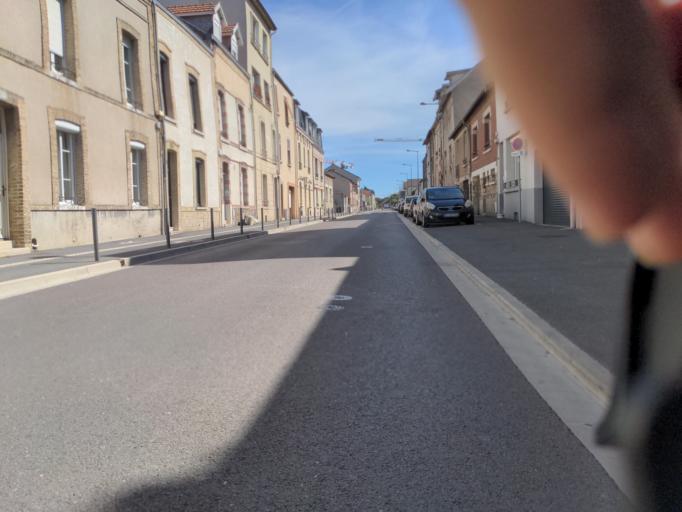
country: FR
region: Champagne-Ardenne
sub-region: Departement de la Marne
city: Reims
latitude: 49.2578
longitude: 4.0578
